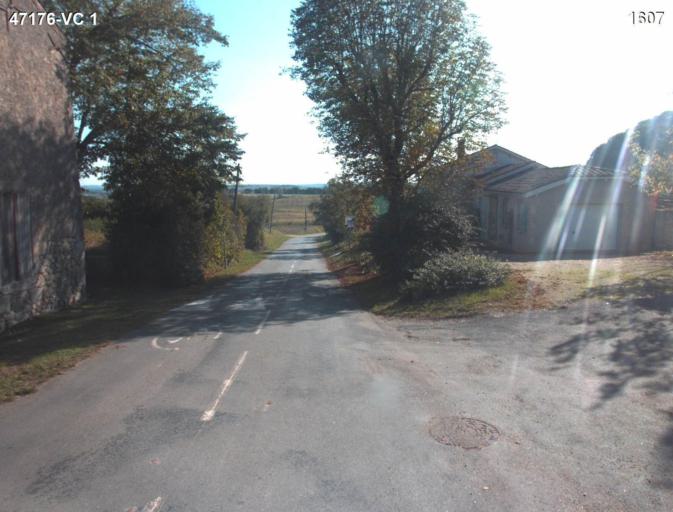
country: FR
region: Aquitaine
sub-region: Departement du Lot-et-Garonne
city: Vianne
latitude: 44.2069
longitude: 0.2944
